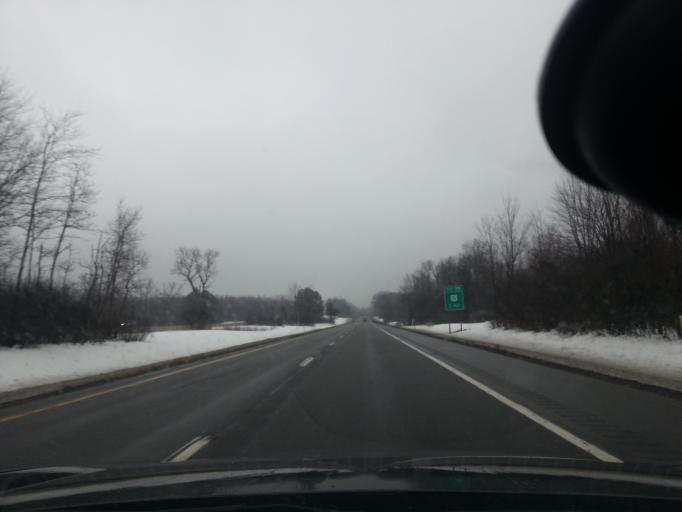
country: US
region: New York
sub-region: Jefferson County
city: Adams
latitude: 43.6940
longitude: -76.0745
